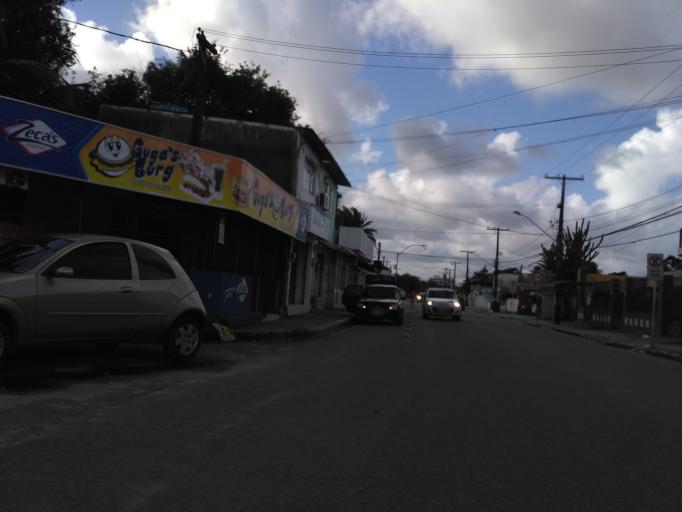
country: BR
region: Pernambuco
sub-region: Recife
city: Recife
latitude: -8.0581
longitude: -34.9423
